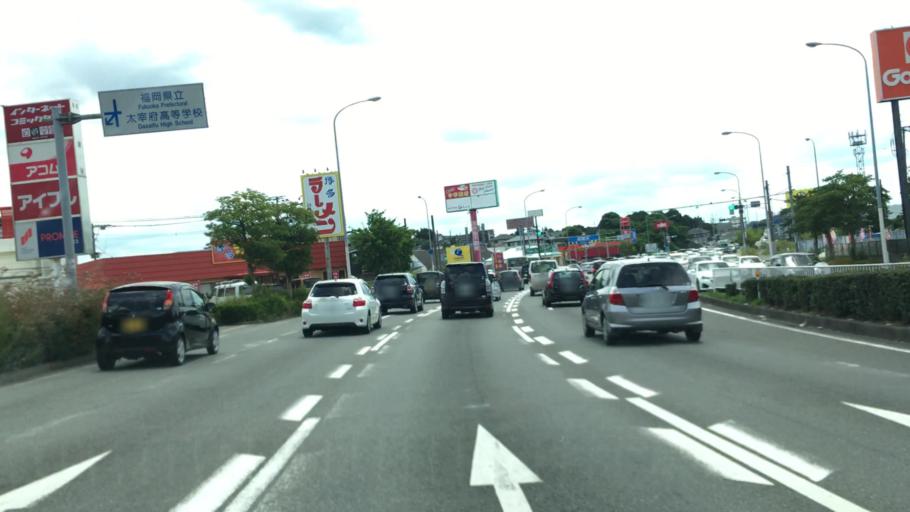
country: JP
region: Fukuoka
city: Chikushino-shi
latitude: 33.4953
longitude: 130.5351
